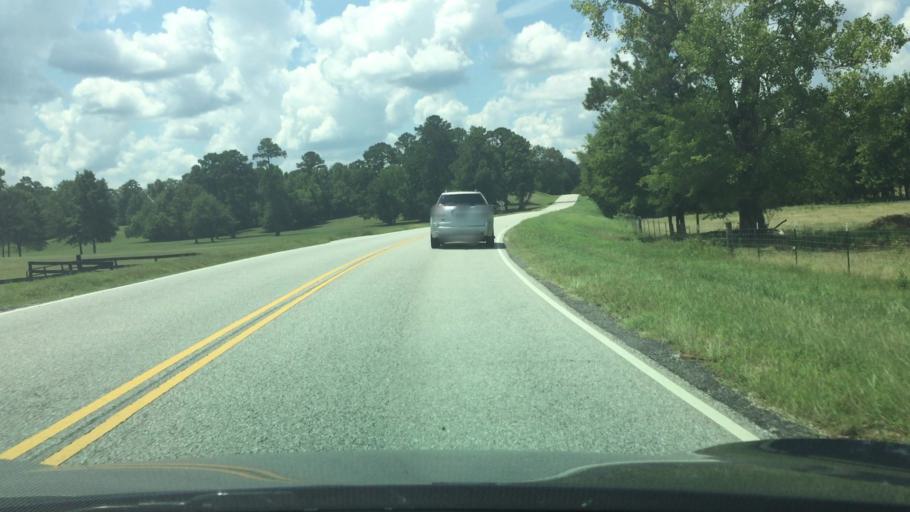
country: US
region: Alabama
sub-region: Montgomery County
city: Pike Road
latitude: 32.2159
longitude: -86.0900
